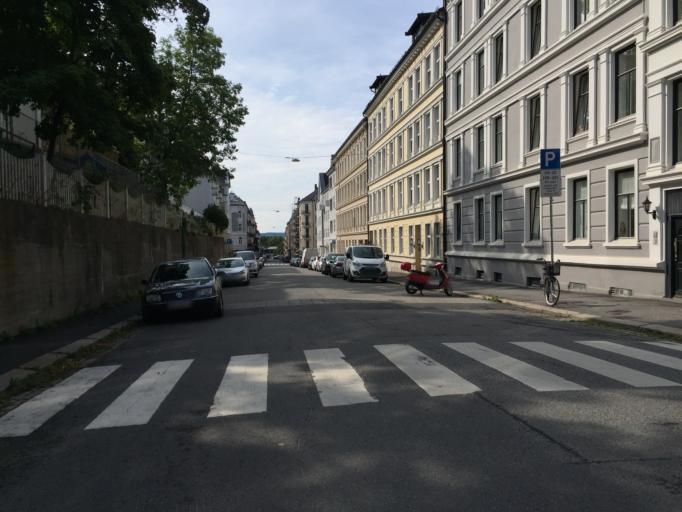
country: NO
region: Oslo
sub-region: Oslo
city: Sjolyststranda
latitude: 59.9213
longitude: 10.7027
